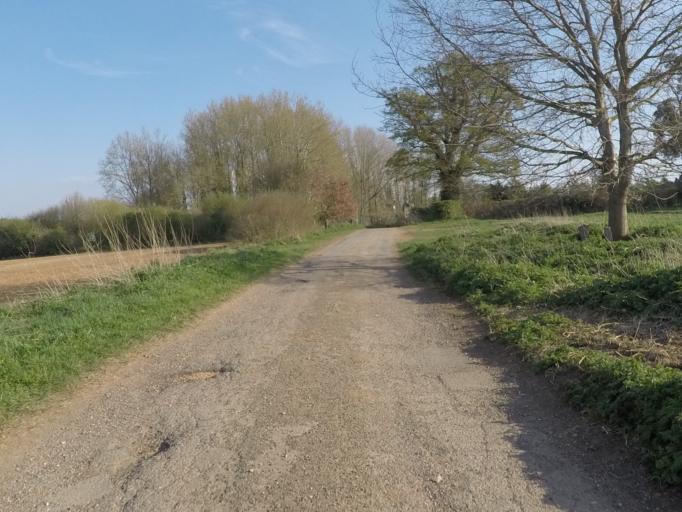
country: GB
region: England
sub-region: Oxfordshire
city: Charlbury
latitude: 51.8734
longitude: -1.4948
